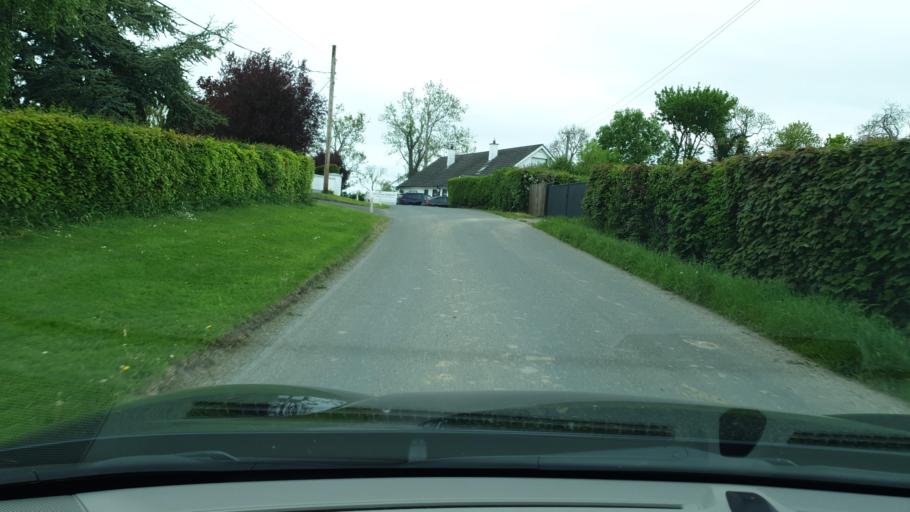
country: IE
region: Leinster
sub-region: An Mhi
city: Ratoath
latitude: 53.4823
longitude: -6.5021
